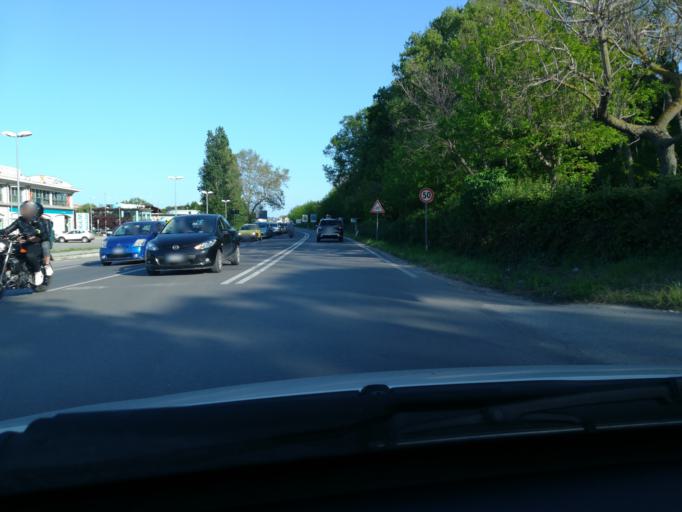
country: IT
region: Emilia-Romagna
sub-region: Provincia di Rimini
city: Misano Adriatico
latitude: 43.9789
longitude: 12.6864
